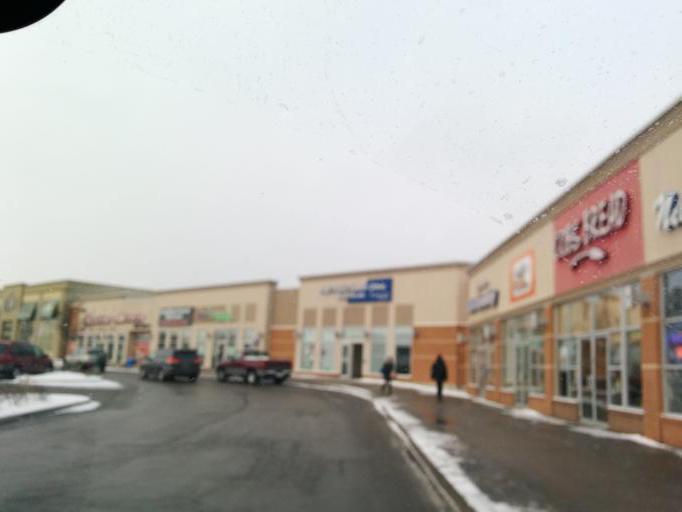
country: CA
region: Ontario
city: Mississauga
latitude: 43.5812
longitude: -79.7577
